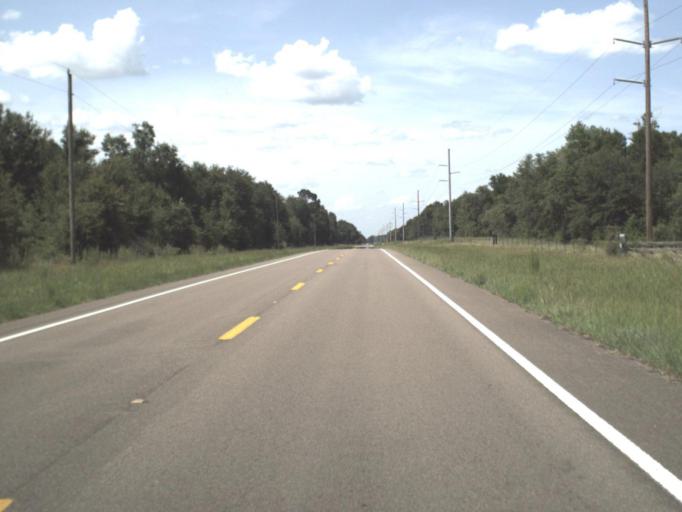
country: US
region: Florida
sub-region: Gilchrist County
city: Trenton
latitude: 29.7081
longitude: -82.7552
